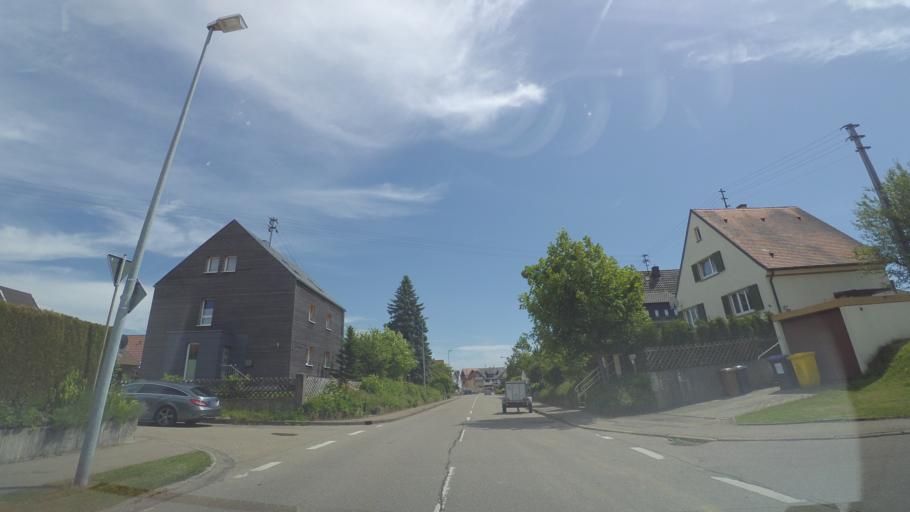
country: DE
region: Baden-Wuerttemberg
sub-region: Regierungsbezirk Stuttgart
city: Kaisersbach
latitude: 48.9318
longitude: 9.6388
